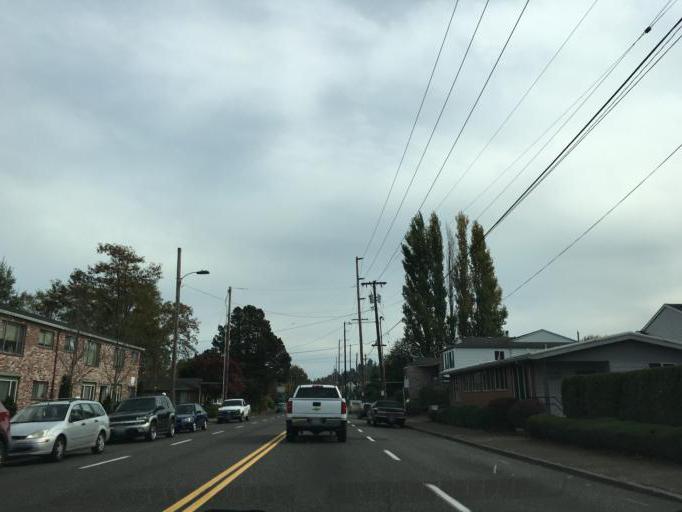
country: US
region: Oregon
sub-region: Multnomah County
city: Lents
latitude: 45.5229
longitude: -122.6121
